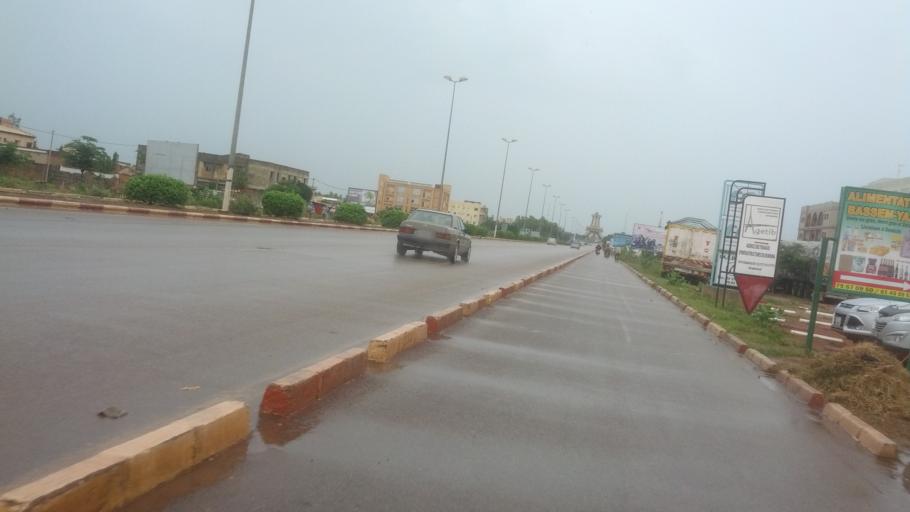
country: BF
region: Centre
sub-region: Kadiogo Province
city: Ouagadougou
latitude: 12.3257
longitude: -1.5027
